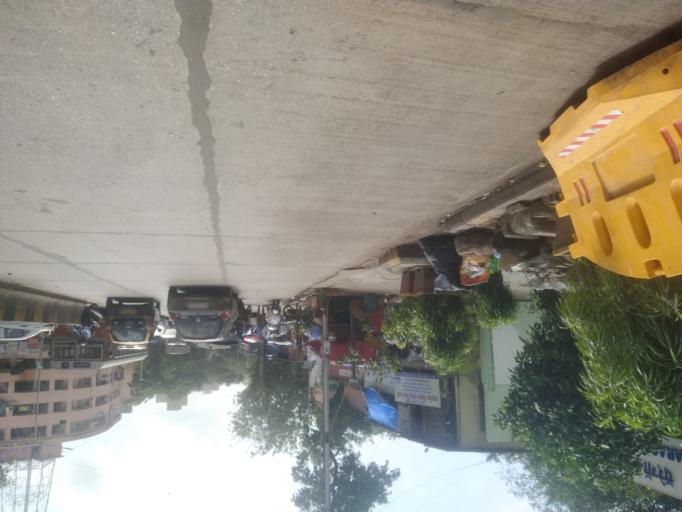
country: IN
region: Maharashtra
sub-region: Mumbai Suburban
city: Mumbai
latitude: 19.0063
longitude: 72.8239
